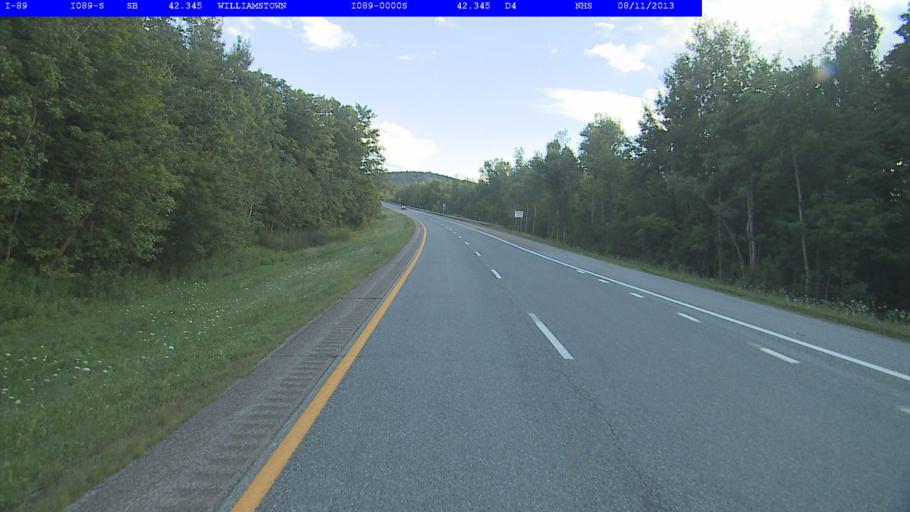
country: US
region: Vermont
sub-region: Washington County
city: Northfield
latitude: 44.1071
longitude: -72.6128
